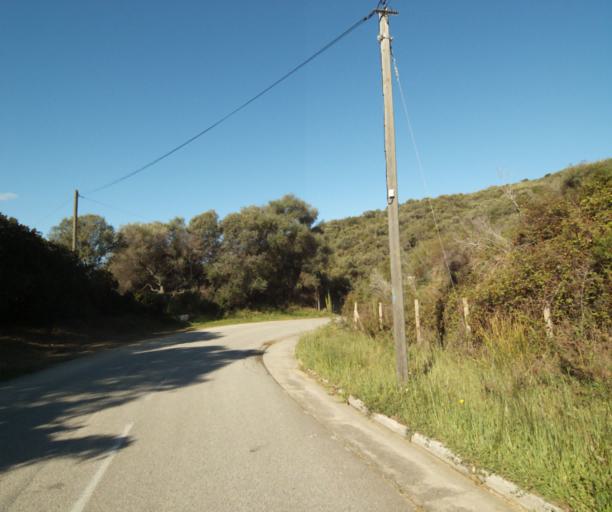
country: FR
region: Corsica
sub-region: Departement de la Corse-du-Sud
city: Propriano
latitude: 41.6664
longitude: 8.8945
